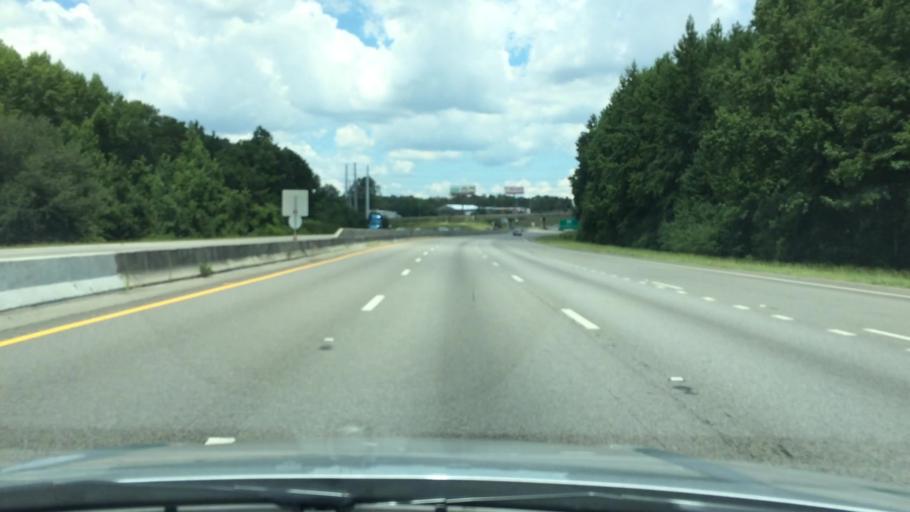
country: US
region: South Carolina
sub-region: Lexington County
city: Cayce
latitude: 33.9363
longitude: -81.0829
